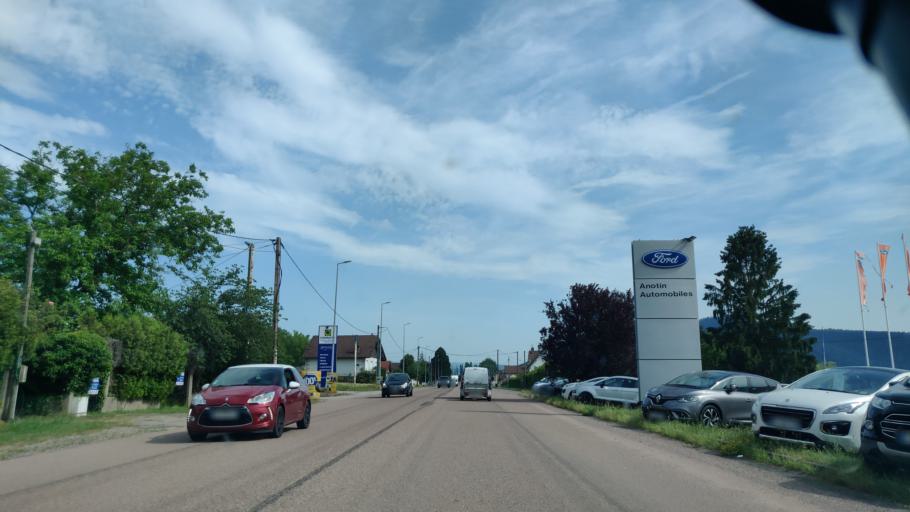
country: FR
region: Lorraine
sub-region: Departement des Vosges
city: Saint-Die-des-Vosges
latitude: 48.3075
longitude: 6.9240
